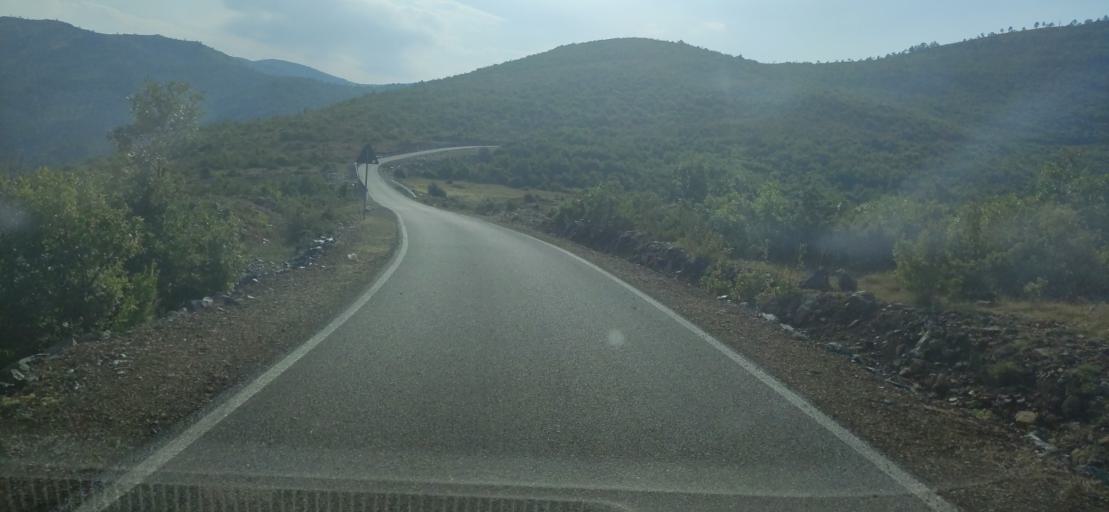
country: AL
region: Shkoder
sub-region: Rrethi i Pukes
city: Iballe
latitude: 42.1735
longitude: 19.9969
